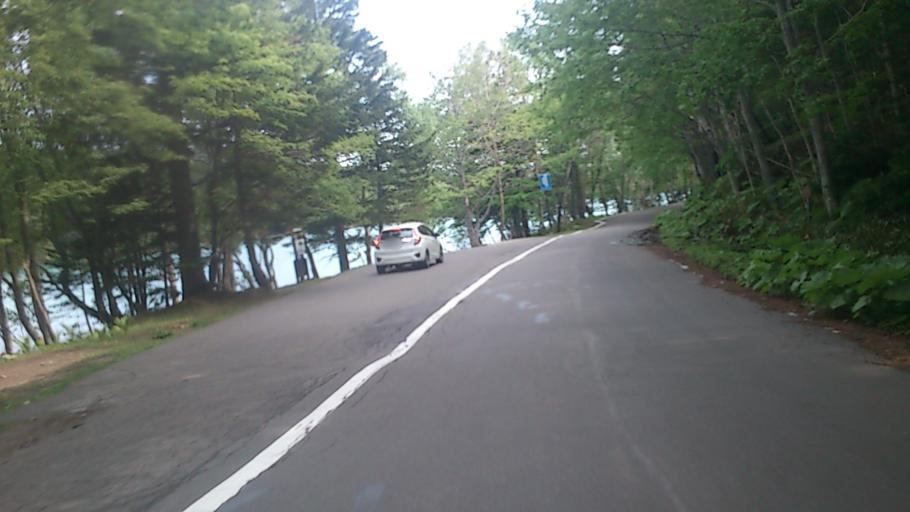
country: JP
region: Hokkaido
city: Kitami
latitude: 43.3898
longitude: 143.9678
